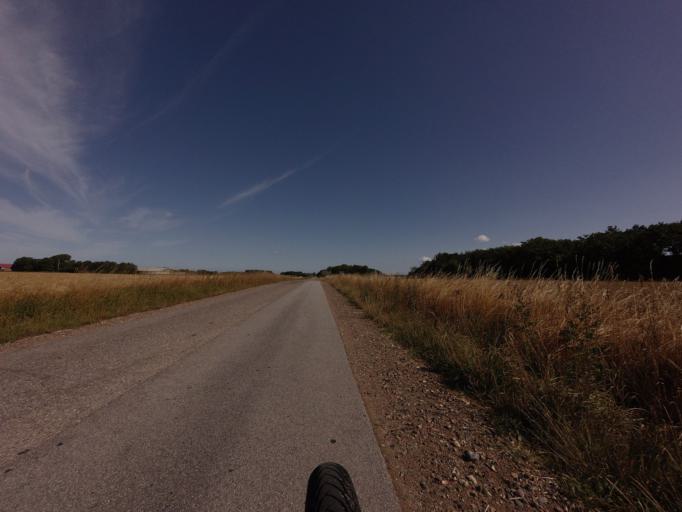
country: DK
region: North Denmark
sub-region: Hjorring Kommune
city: Vra
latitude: 57.3973
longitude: 9.9541
